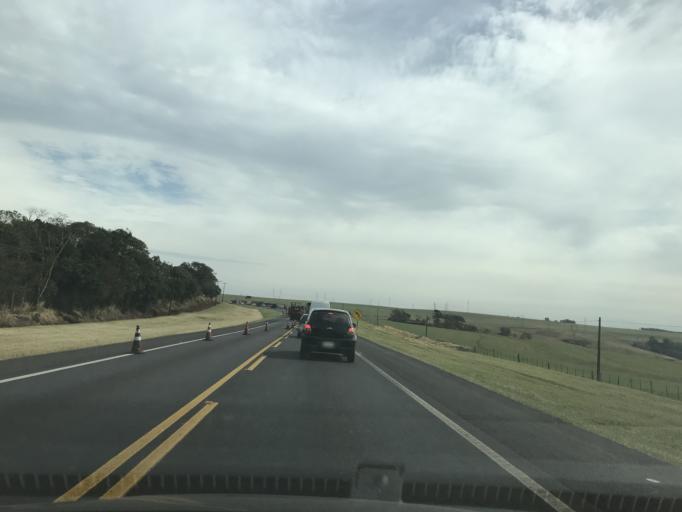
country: BR
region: Parana
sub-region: Cascavel
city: Cascavel
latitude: -25.0741
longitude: -53.6848
